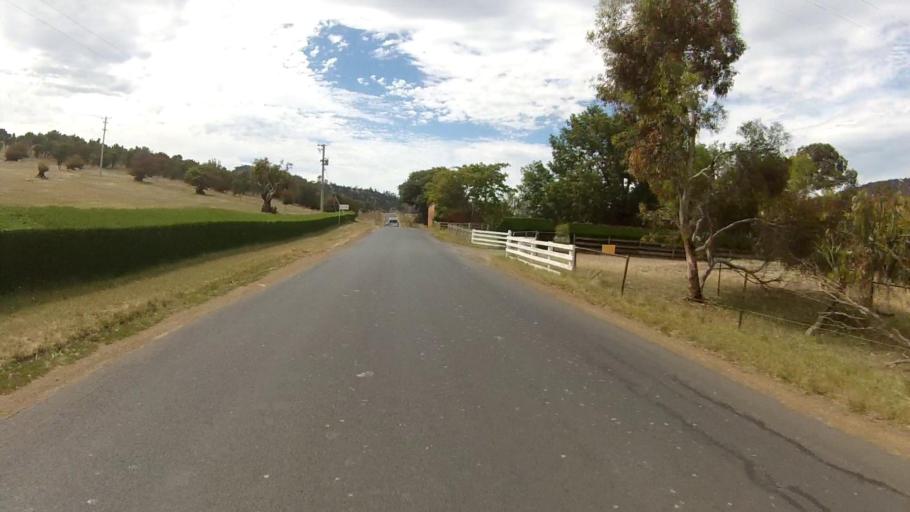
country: AU
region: Tasmania
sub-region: Brighton
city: Old Beach
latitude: -42.7185
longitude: 147.3293
